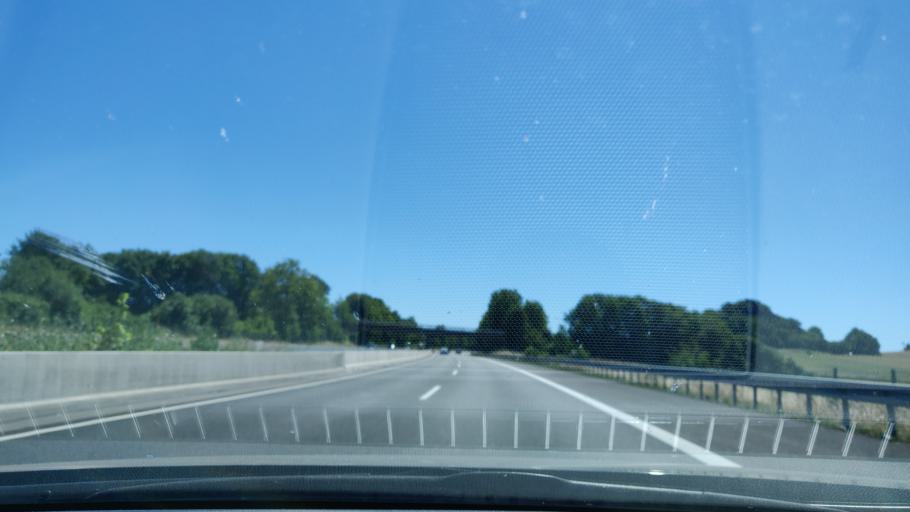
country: DE
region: Hesse
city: Gudensberg
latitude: 51.1964
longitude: 9.3986
